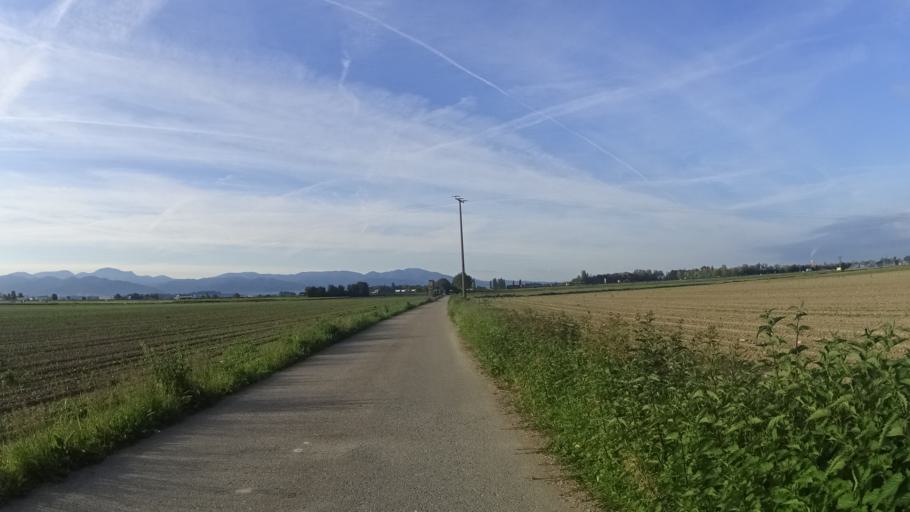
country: DE
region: Baden-Wuerttemberg
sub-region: Freiburg Region
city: Hartheim
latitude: 47.9516
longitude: 7.6465
